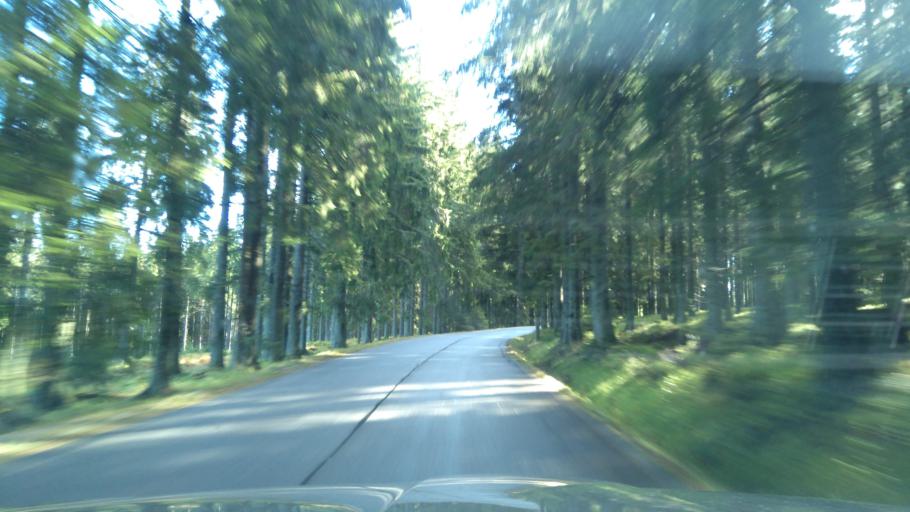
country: CZ
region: Jihocesky
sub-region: Okres Prachatice
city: Borova Lada
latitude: 49.0253
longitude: 13.5566
